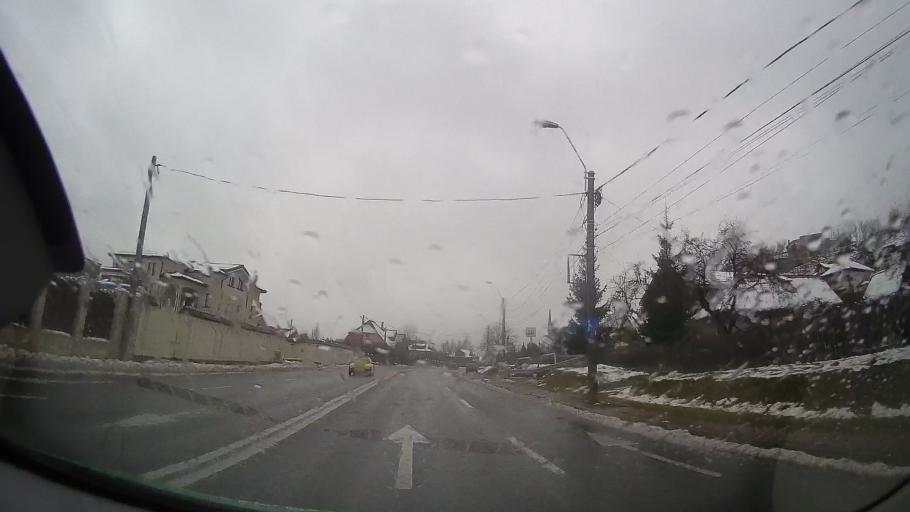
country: RO
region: Neamt
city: Piatra Neamt
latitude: 46.9403
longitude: 26.3241
